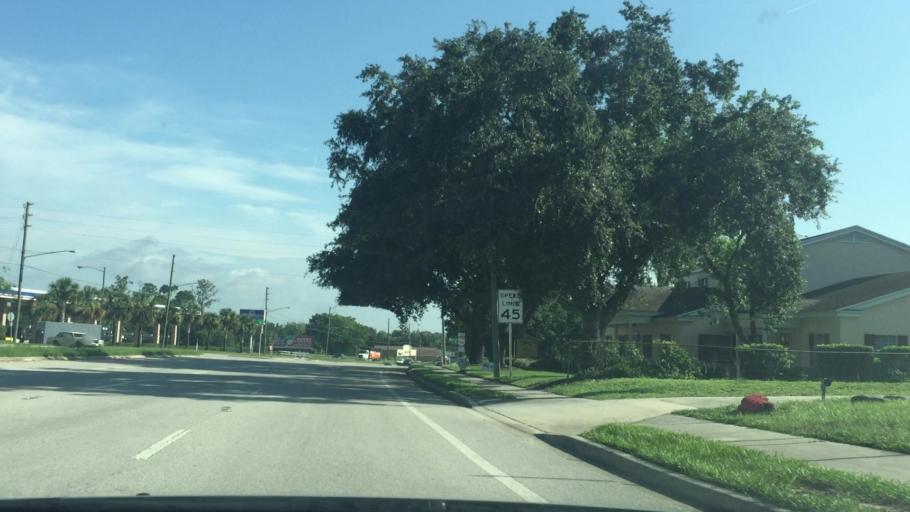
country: US
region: Florida
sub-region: Orange County
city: Orlovista
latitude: 28.5443
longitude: -81.4582
